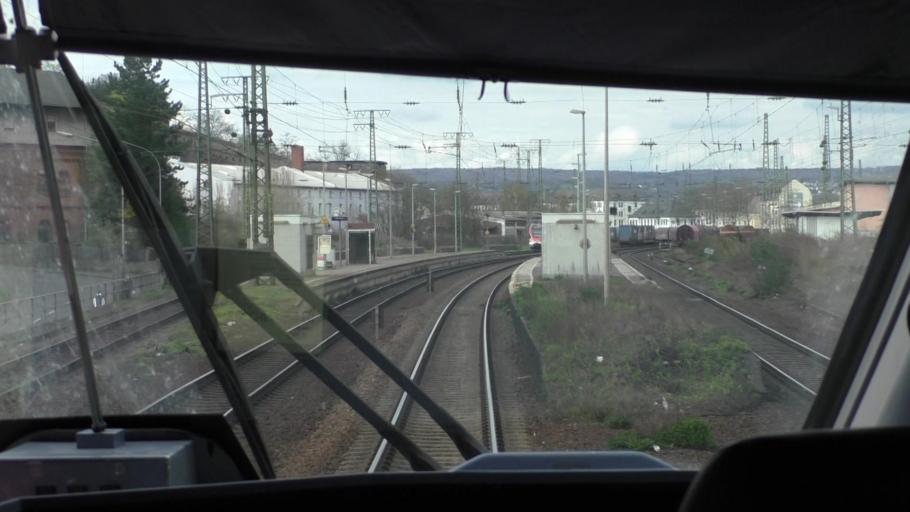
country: DE
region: Rheinland-Pfalz
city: Koblenz
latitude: 50.3662
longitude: 7.5912
